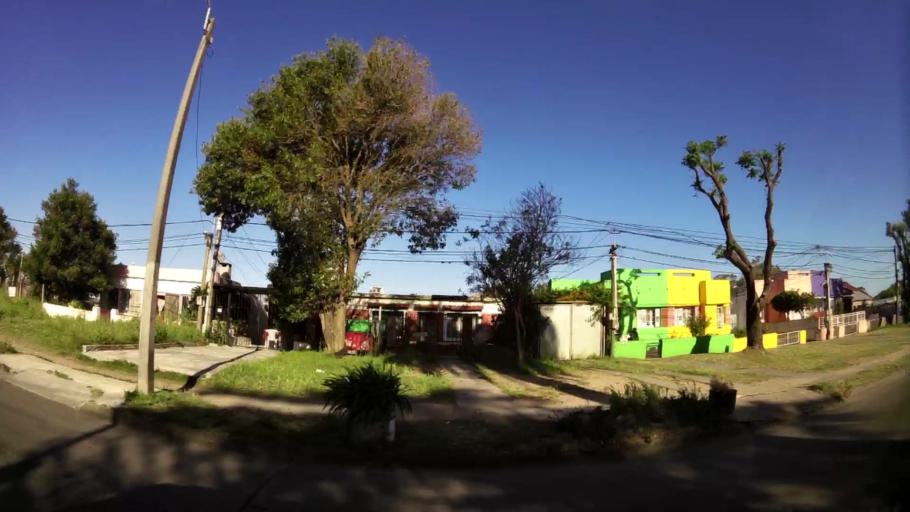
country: UY
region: Canelones
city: La Paz
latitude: -34.8289
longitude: -56.2006
